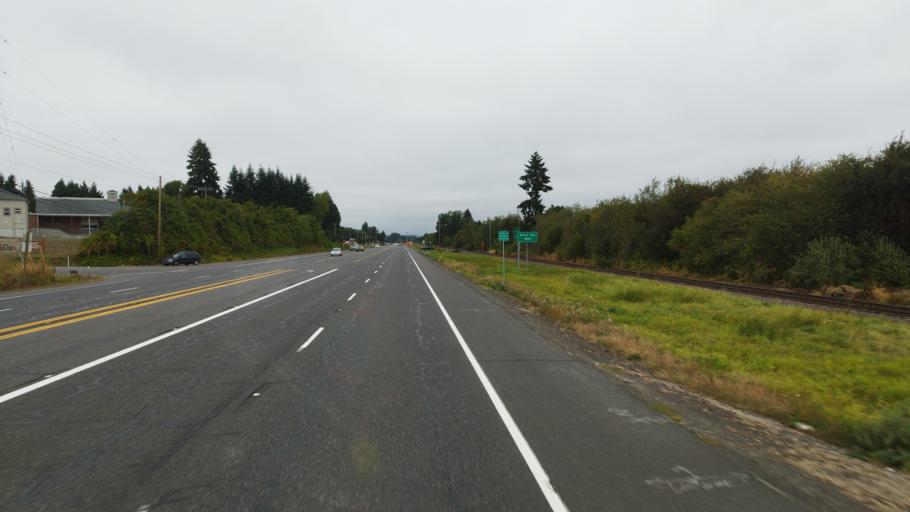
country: US
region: Oregon
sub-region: Columbia County
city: Warren
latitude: 45.8111
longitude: -122.8547
